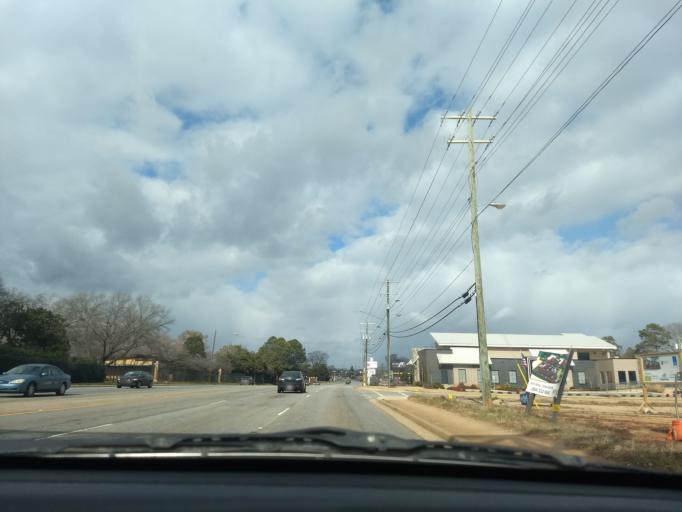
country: US
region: South Carolina
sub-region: Greenville County
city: Wade Hampton
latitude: 34.8742
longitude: -82.3592
